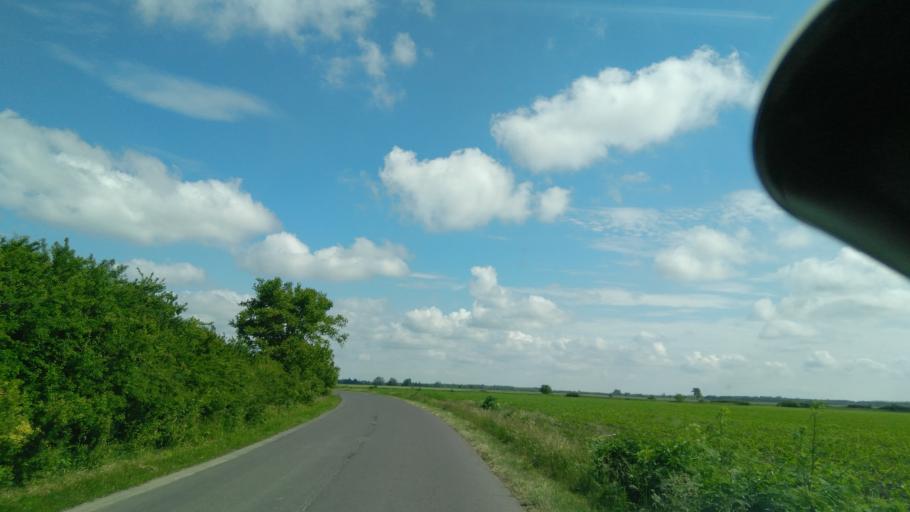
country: HU
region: Bekes
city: Bekes
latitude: 46.8159
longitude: 21.1488
